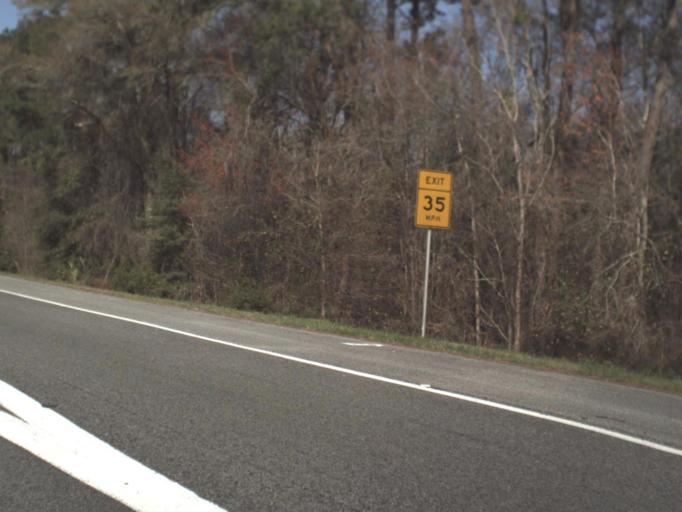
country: US
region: Florida
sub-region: Jefferson County
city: Monticello
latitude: 30.4890
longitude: -84.0205
